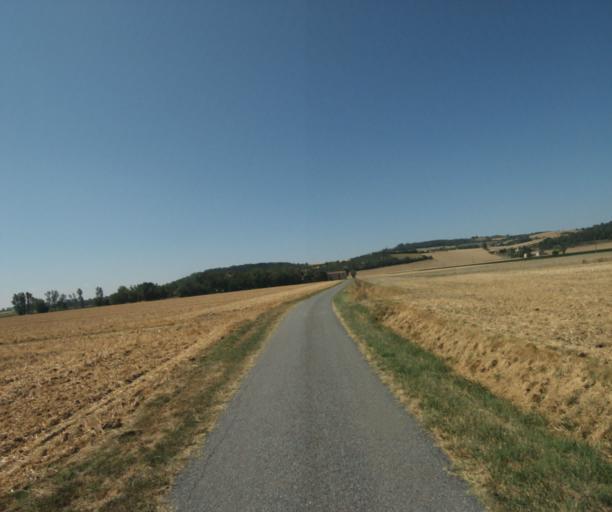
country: FR
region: Midi-Pyrenees
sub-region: Departement du Tarn
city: Puylaurens
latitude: 43.5228
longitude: 1.9536
